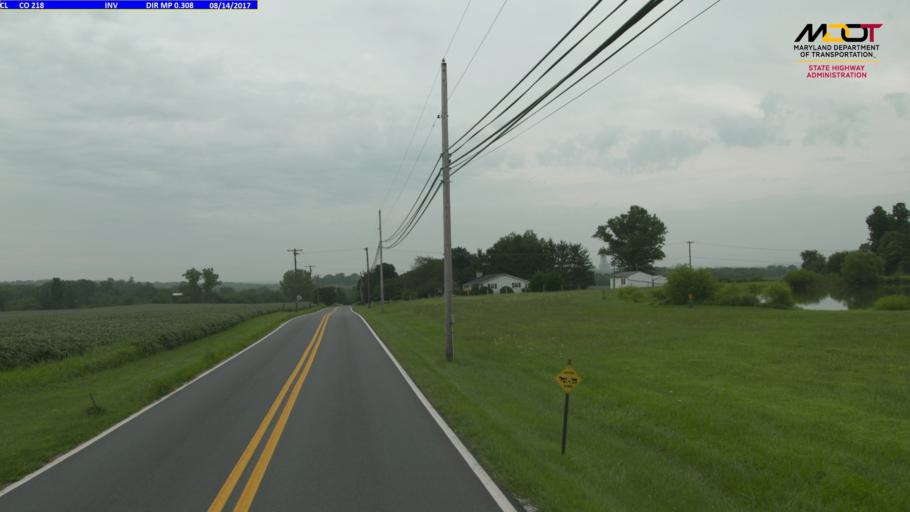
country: US
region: Maryland
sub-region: Carroll County
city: Taneytown
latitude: 39.5900
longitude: -77.1836
